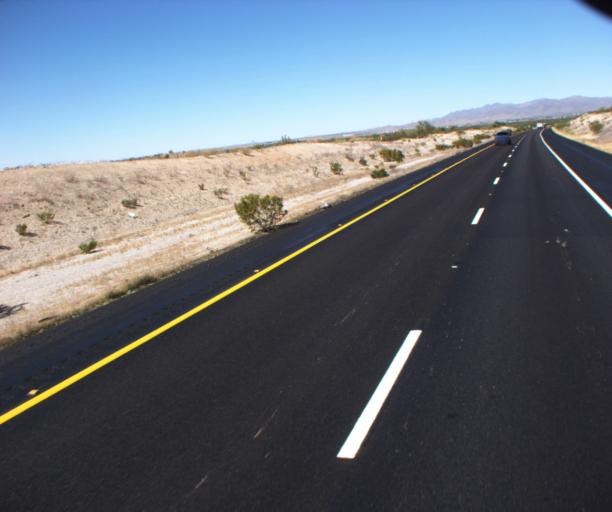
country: US
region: Arizona
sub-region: Maricopa County
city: Buckeye
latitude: 33.3100
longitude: -112.6248
